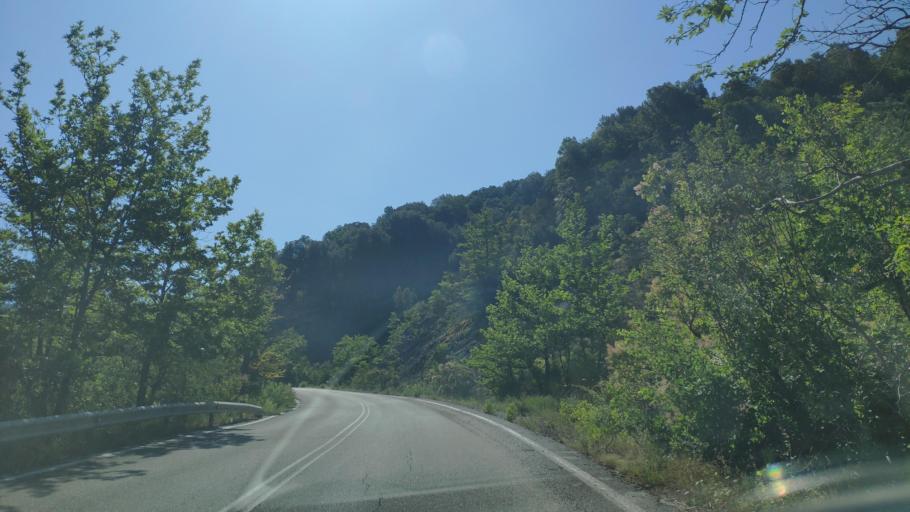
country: GR
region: West Greece
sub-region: Nomos Aitolias kai Akarnanias
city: Sardinia
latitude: 38.9250
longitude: 21.3867
